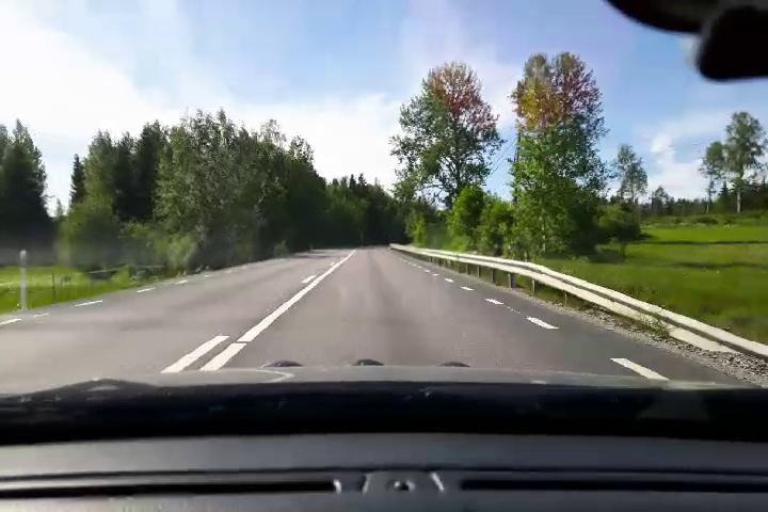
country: SE
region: Gaevleborg
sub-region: Bollnas Kommun
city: Kilafors
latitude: 61.1724
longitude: 16.8028
